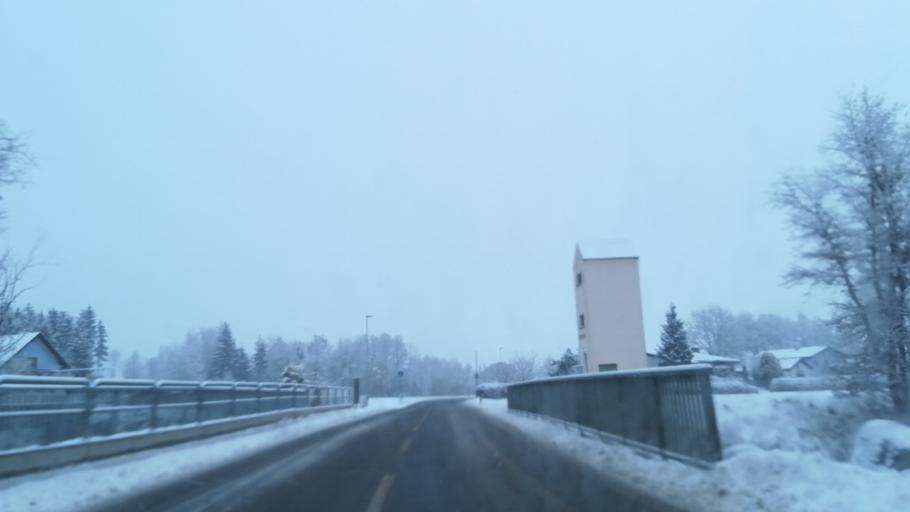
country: AT
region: Styria
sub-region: Politischer Bezirk Murtal
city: Spielberg bei Knittelfeld
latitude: 47.2164
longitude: 14.7933
